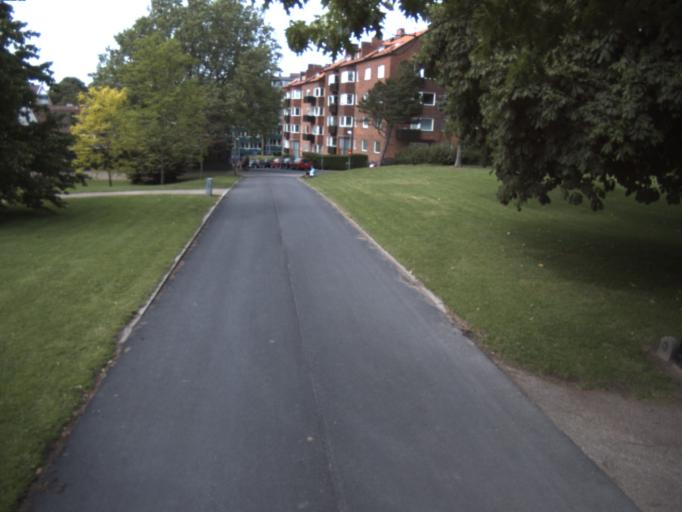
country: SE
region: Skane
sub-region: Helsingborg
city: Helsingborg
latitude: 56.0487
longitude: 12.6979
